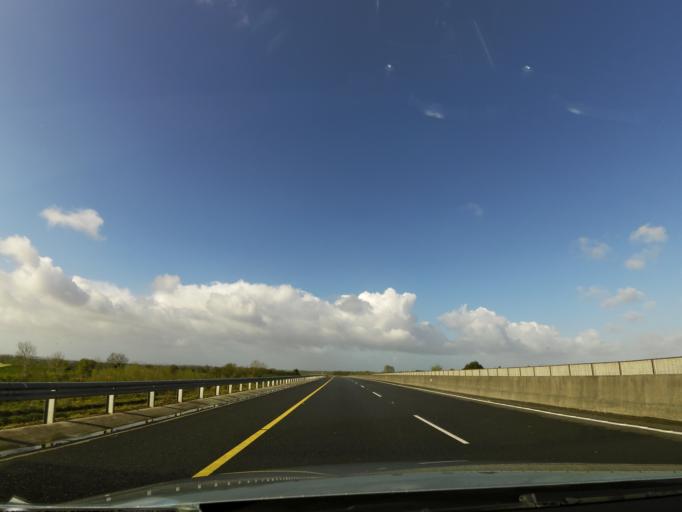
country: IE
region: Munster
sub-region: County Limerick
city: Castleconnell
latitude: 52.7326
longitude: -8.4557
